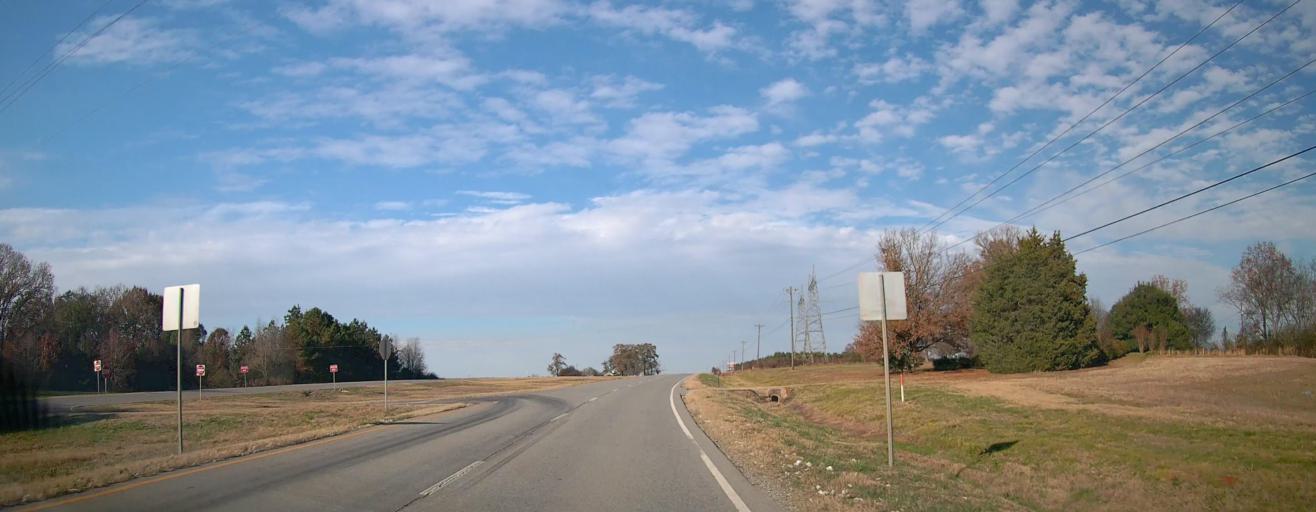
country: US
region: Alabama
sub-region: Morgan County
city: Decatur
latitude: 34.6933
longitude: -86.9553
